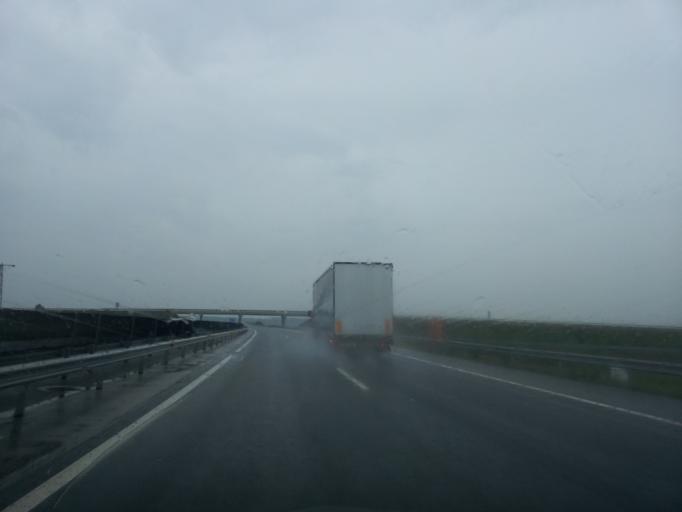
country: HU
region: Tolna
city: Ocseny
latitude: 46.3382
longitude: 18.7569
